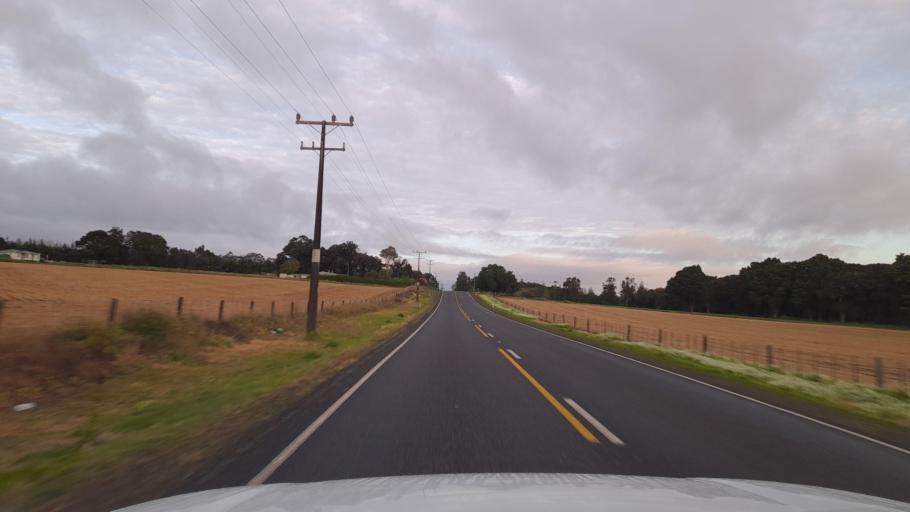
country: NZ
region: Northland
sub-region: Whangarei
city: Maungatapere
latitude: -35.7511
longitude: 174.1678
